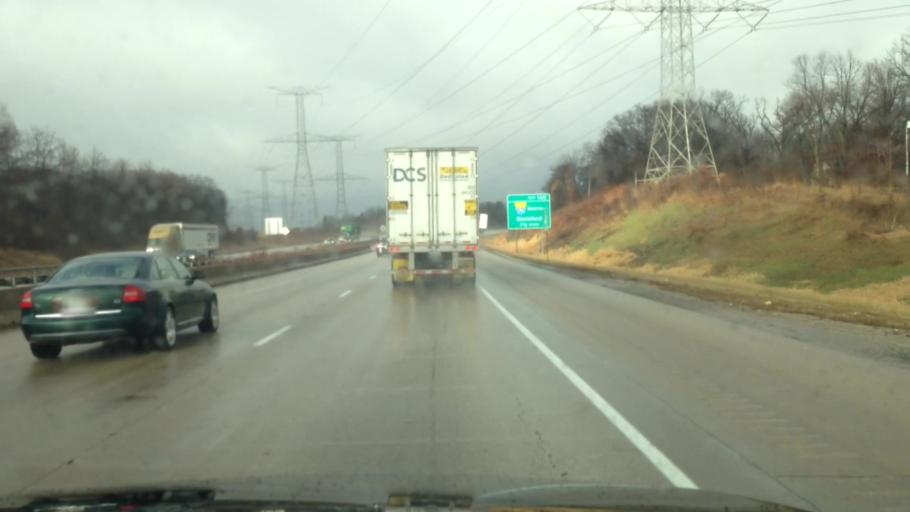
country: US
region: Illinois
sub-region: Will County
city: New Lenox
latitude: 41.5234
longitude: -87.9904
